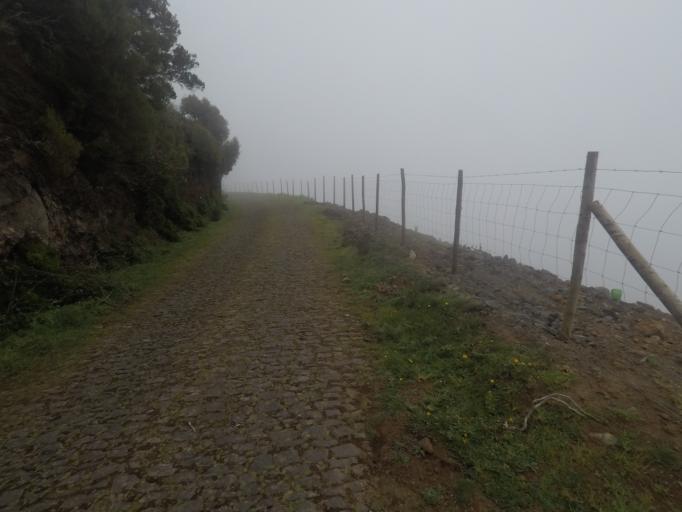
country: PT
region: Madeira
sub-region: Calheta
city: Arco da Calheta
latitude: 32.7330
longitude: -17.0969
